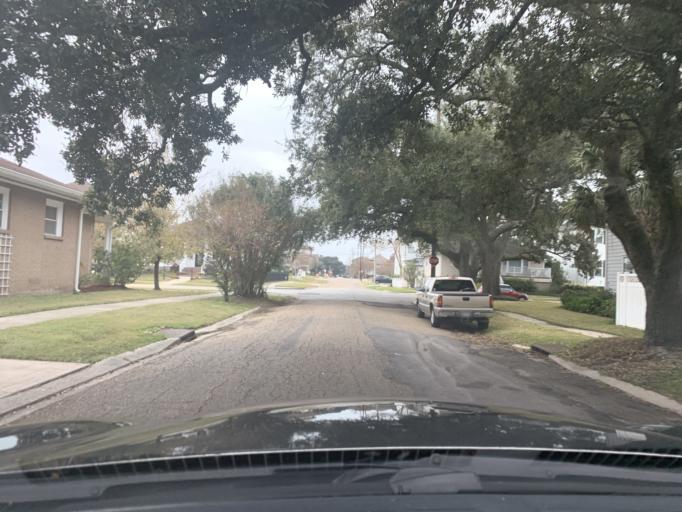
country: US
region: Louisiana
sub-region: Jefferson Parish
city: Metairie
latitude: 30.0157
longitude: -90.1050
